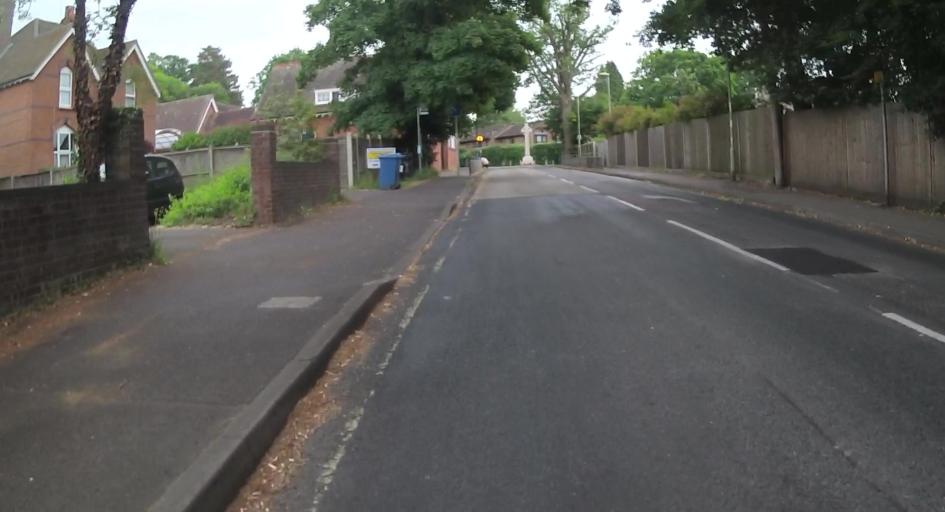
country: GB
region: England
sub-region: Hampshire
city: Fleet
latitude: 51.2609
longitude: -0.8461
